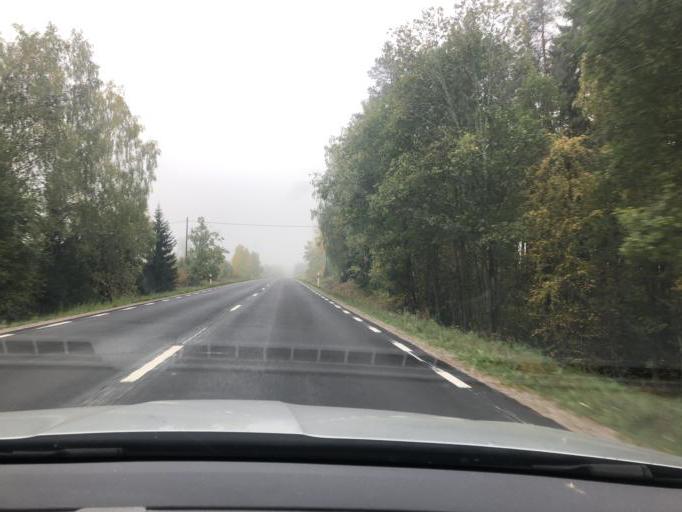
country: SE
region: Uppsala
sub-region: Tierps Kommun
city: Orbyhus
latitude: 60.2429
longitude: 17.6577
